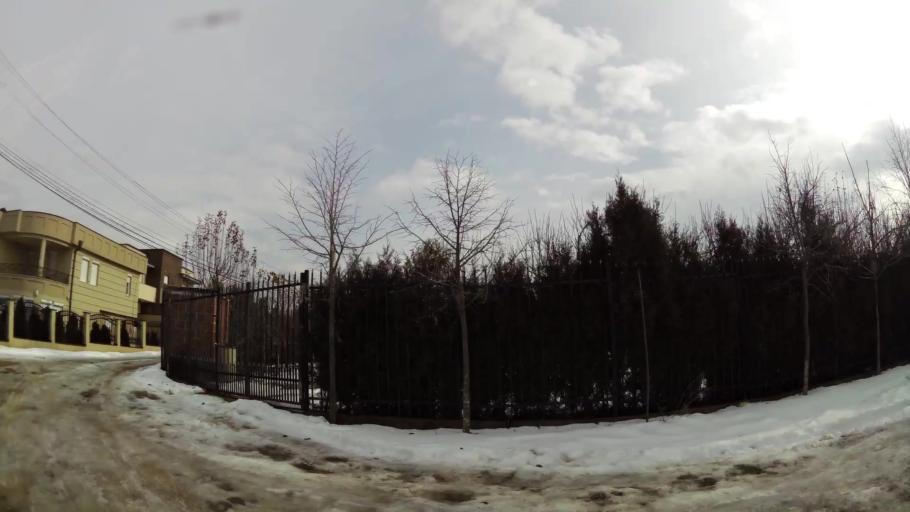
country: XK
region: Pristina
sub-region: Komuna e Prishtines
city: Pristina
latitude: 42.6940
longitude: 21.1678
